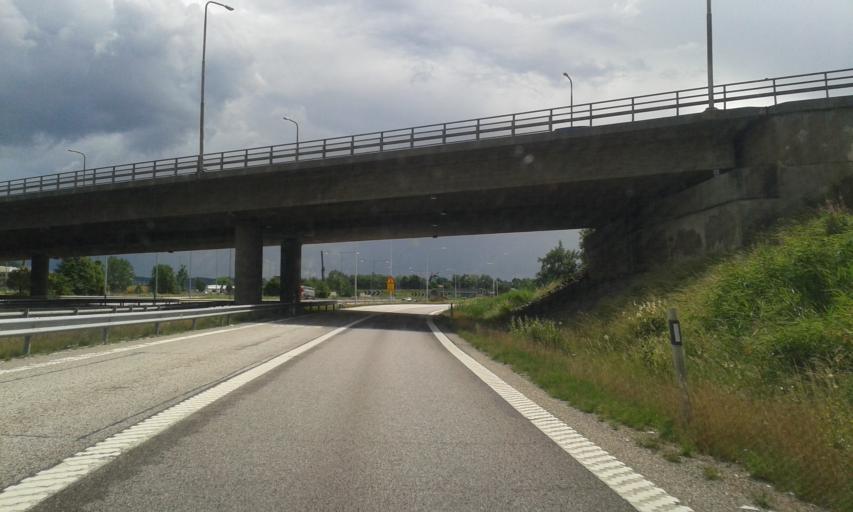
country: SE
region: Vaestra Goetaland
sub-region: Kungalvs Kommun
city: Kungalv
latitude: 57.8757
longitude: 11.9627
